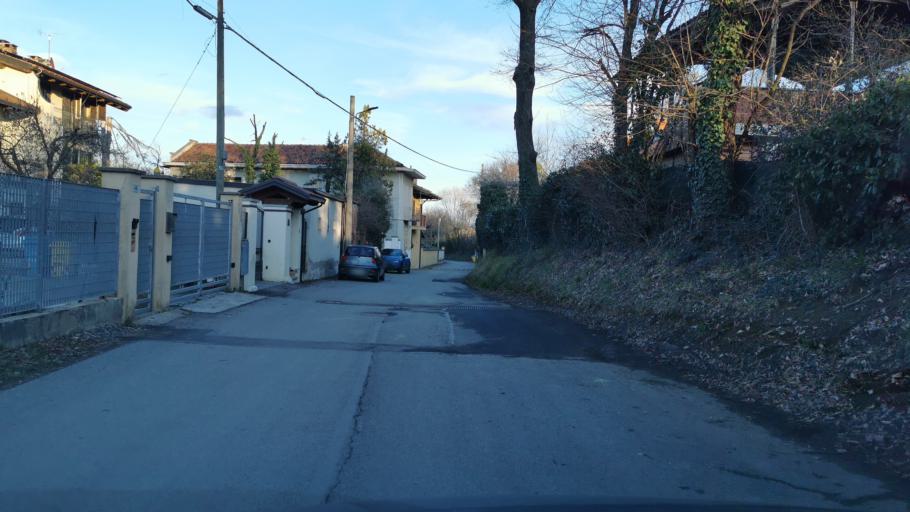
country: IT
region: Piedmont
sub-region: Provincia di Torino
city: Rivarossa
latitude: 45.2521
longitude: 7.7087
